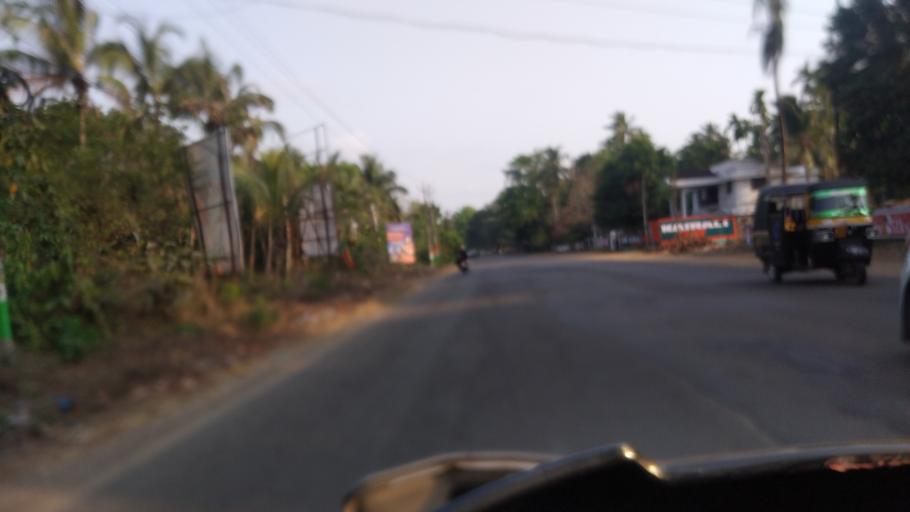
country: IN
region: Kerala
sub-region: Thrissur District
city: Thanniyam
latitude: 10.4355
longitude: 76.0977
